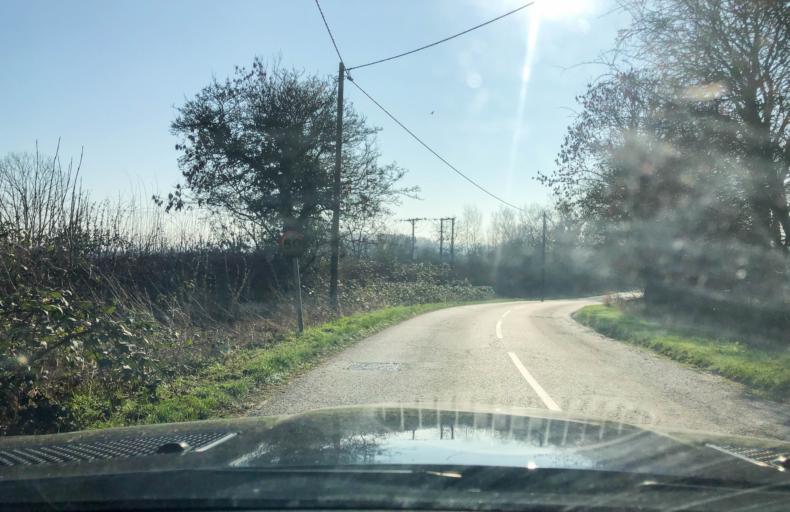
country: GB
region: England
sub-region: Warwickshire
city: Wellesbourne Mountford
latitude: 52.1638
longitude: -1.5127
